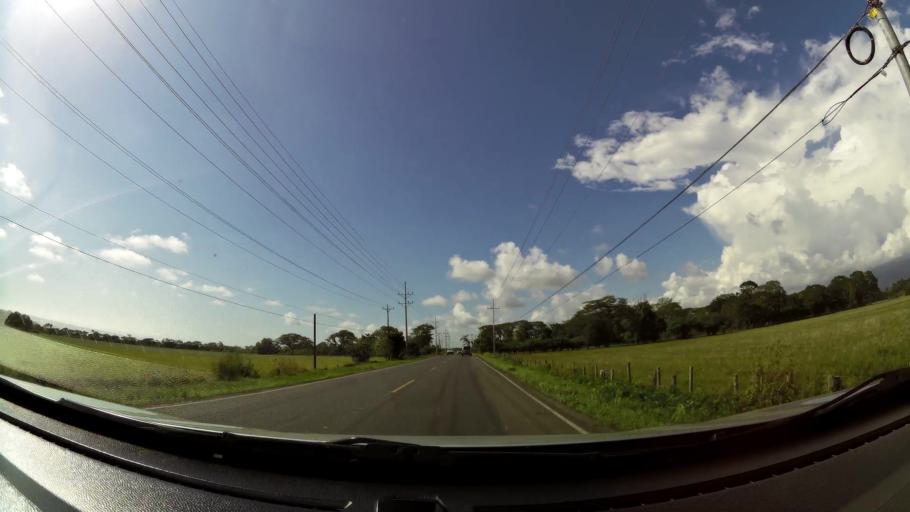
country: CR
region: Puntarenas
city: Quepos
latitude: 9.4536
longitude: -84.1720
